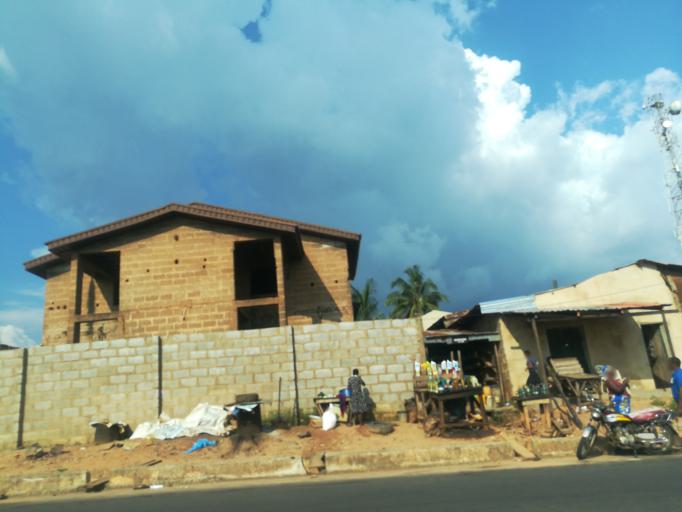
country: NG
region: Oyo
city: Ibadan
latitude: 7.4213
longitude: 3.8446
